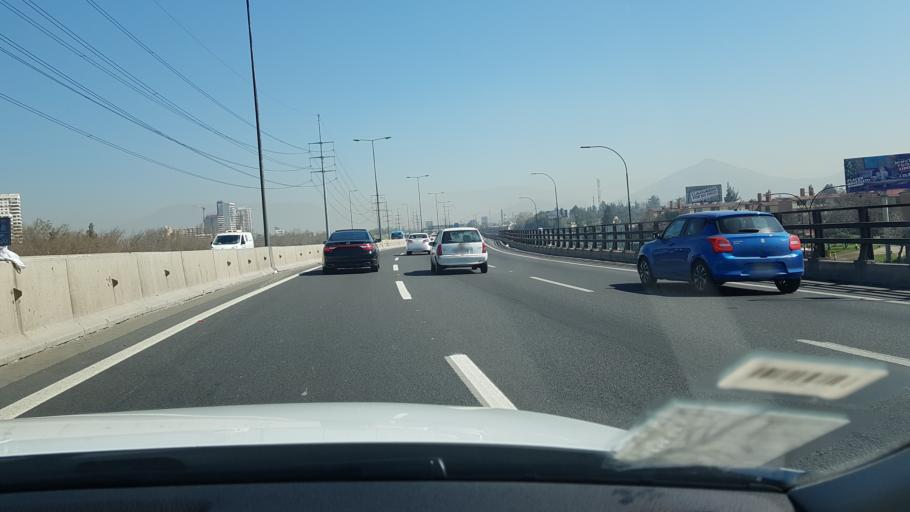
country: CL
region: Santiago Metropolitan
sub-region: Provincia de Santiago
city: Santiago
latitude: -33.4288
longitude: -70.6637
